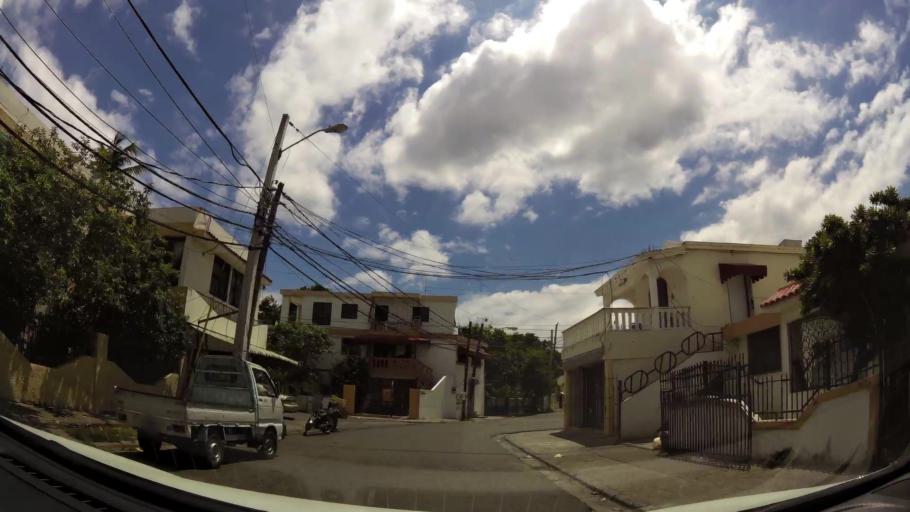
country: DO
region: Nacional
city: Bella Vista
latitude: 18.4346
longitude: -69.9590
